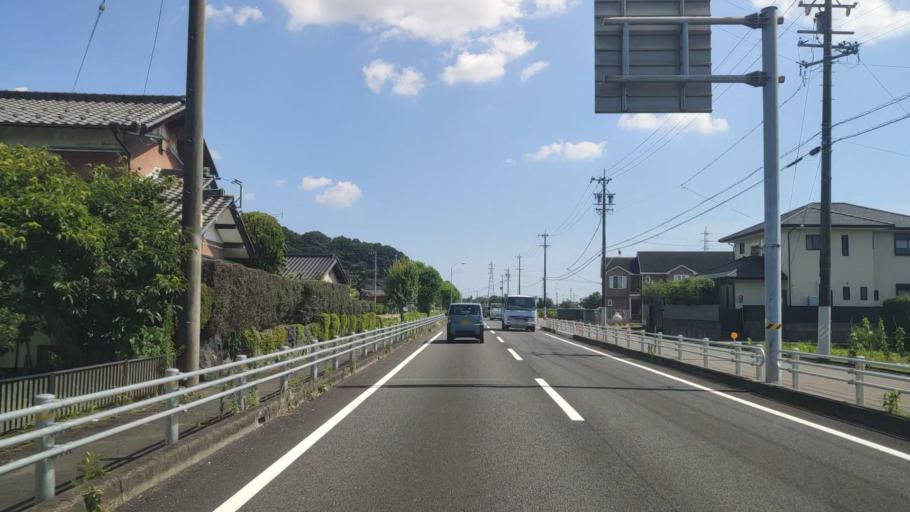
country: JP
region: Gifu
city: Godo
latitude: 35.4793
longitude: 136.6749
